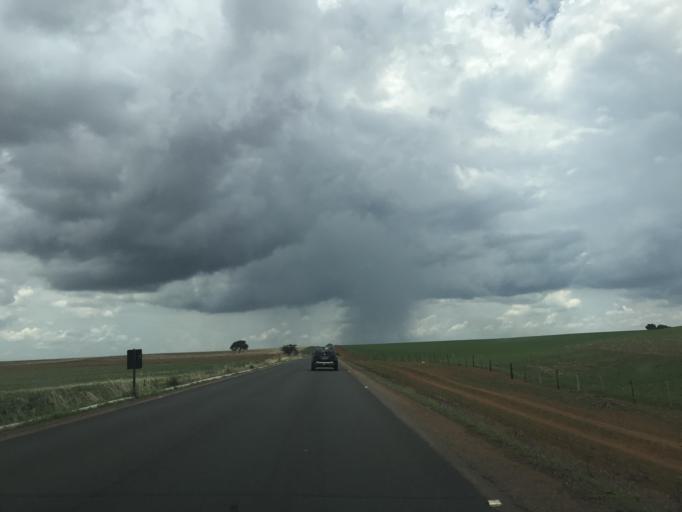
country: BR
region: Goias
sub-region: Vianopolis
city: Vianopolis
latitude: -16.8174
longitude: -48.5240
